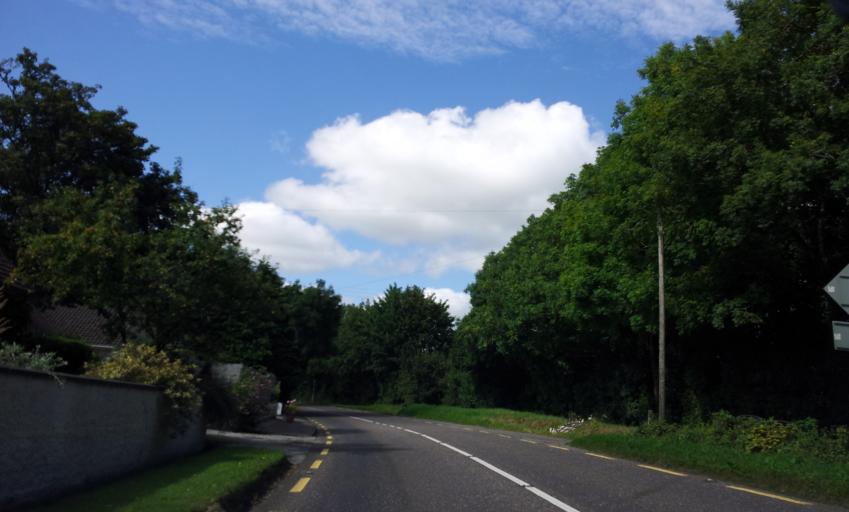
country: IE
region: Munster
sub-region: County Cork
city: Macroom
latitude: 51.8851
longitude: -8.9328
